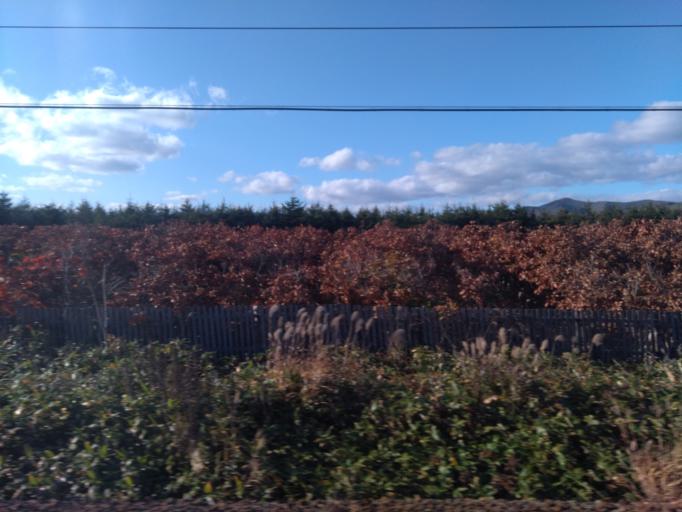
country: JP
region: Hokkaido
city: Niseko Town
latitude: 42.5468
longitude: 140.4132
